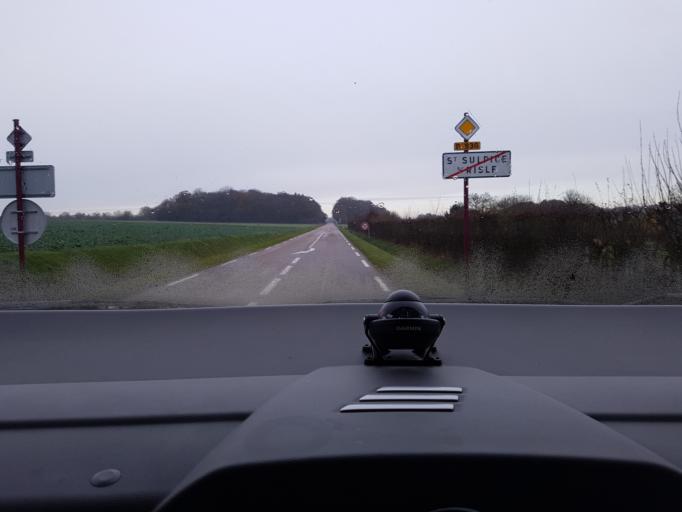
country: FR
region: Lower Normandy
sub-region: Departement de l'Orne
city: Saint-Sulpice-sur-Risle
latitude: 48.7814
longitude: 0.6567
